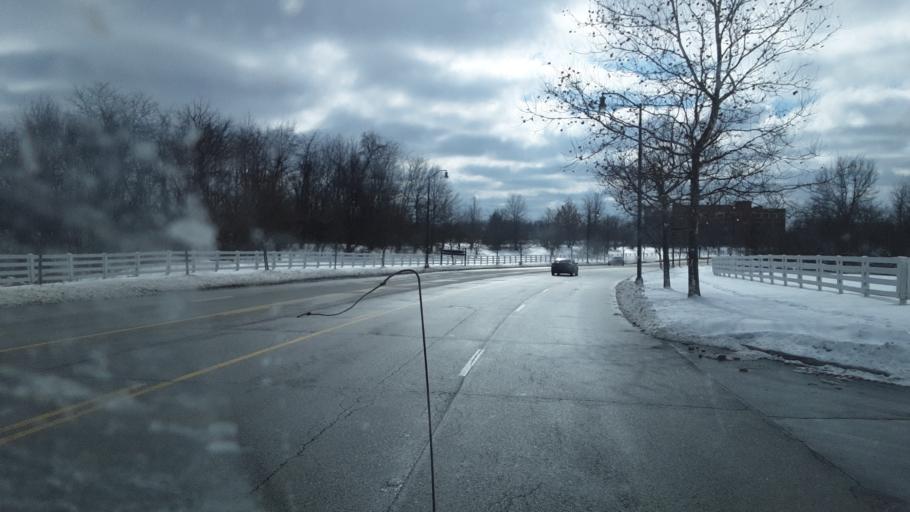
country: US
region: Ohio
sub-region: Franklin County
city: New Albany
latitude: 40.0968
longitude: -82.8178
